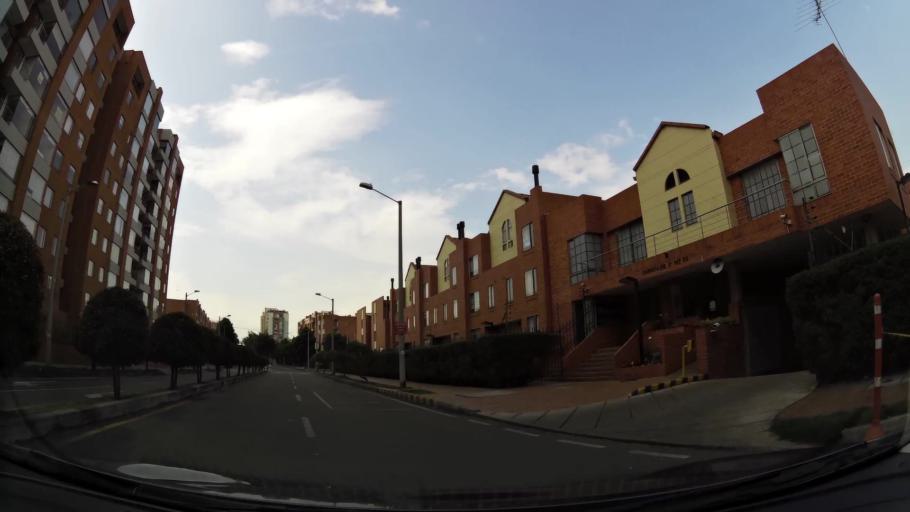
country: CO
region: Bogota D.C.
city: Barrio San Luis
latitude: 4.7339
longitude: -74.0602
